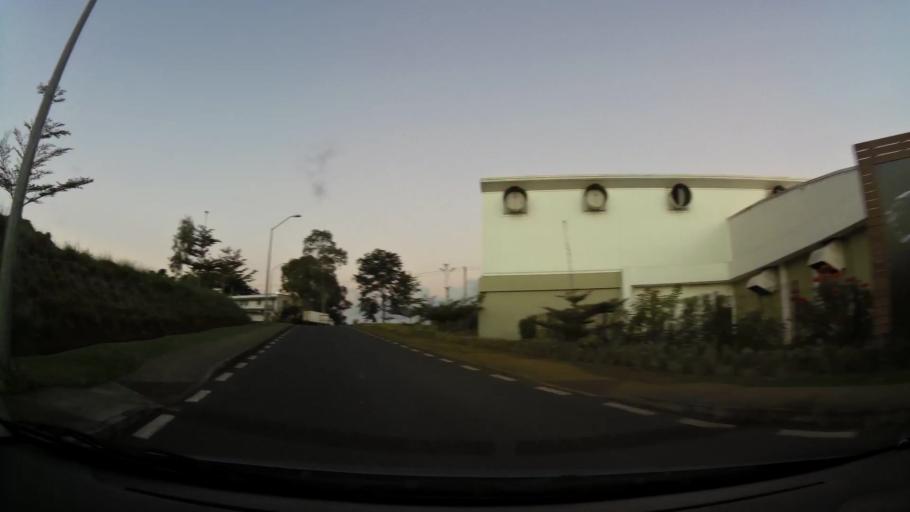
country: MU
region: Moka
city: Moka
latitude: -20.2254
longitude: 57.4990
